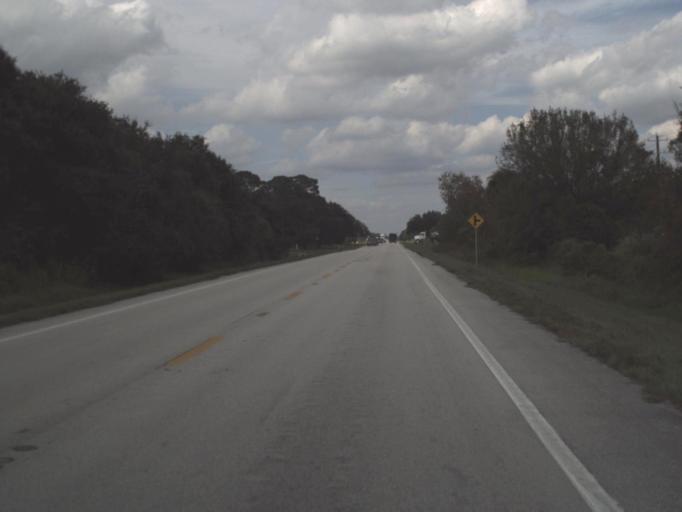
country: US
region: Florida
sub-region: Okeechobee County
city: Cypress Quarters
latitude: 27.3288
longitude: -80.8239
